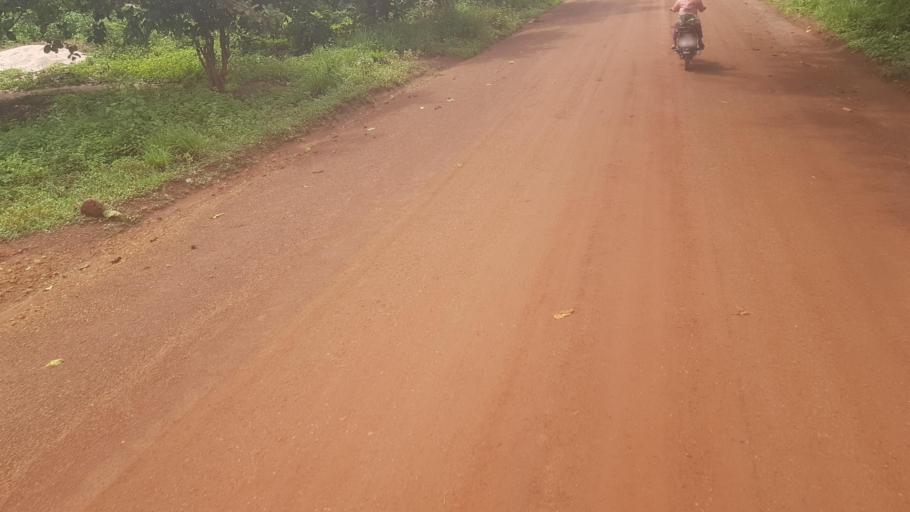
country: SL
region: Southern Province
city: Mogbwemo
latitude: 7.7518
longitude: -12.3084
